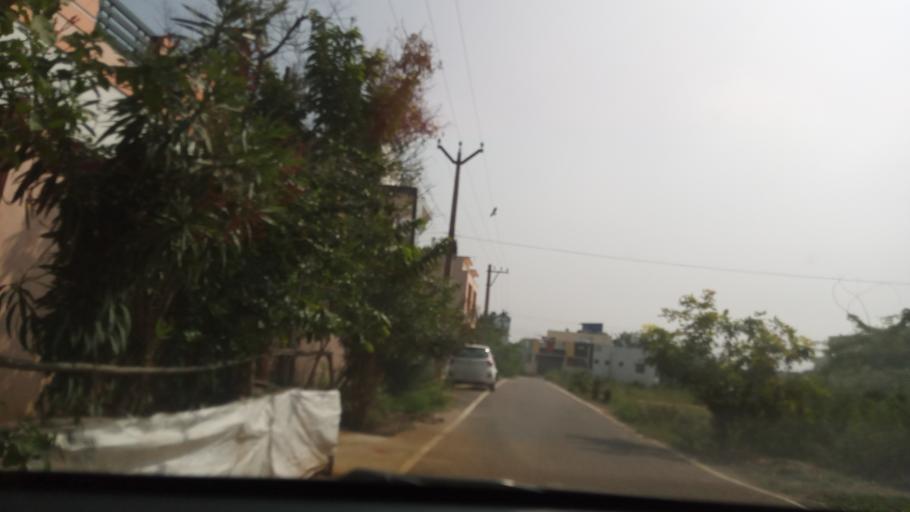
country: IN
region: Tamil Nadu
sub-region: Coimbatore
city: Perur
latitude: 11.0066
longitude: 76.8902
